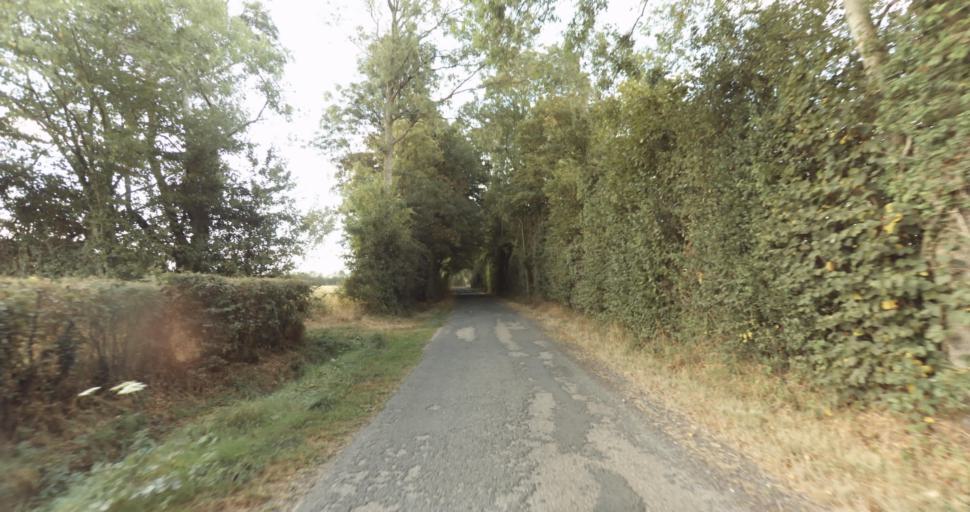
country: FR
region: Lower Normandy
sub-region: Departement de l'Orne
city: Vimoutiers
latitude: 48.9483
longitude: 0.2403
